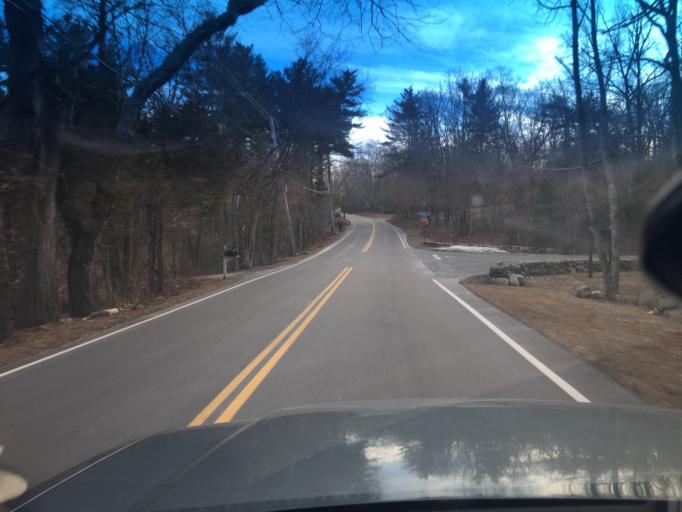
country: US
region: Massachusetts
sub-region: Middlesex County
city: Holliston
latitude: 42.1773
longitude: -71.4114
